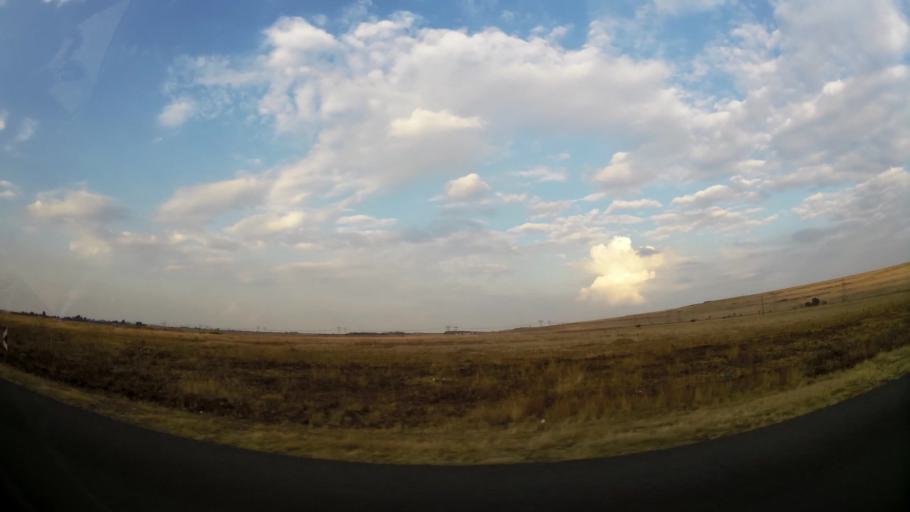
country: ZA
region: Gauteng
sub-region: Sedibeng District Municipality
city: Vanderbijlpark
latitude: -26.6278
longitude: 27.8098
